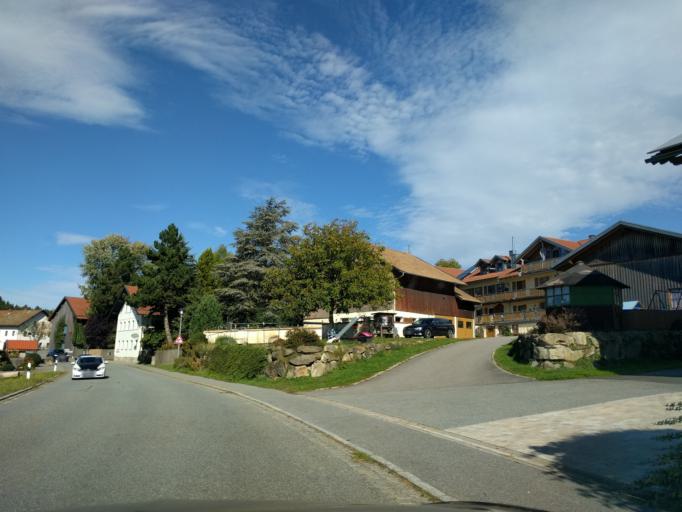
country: DE
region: Bavaria
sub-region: Upper Palatinate
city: Kotzting
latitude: 49.1443
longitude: 12.8860
